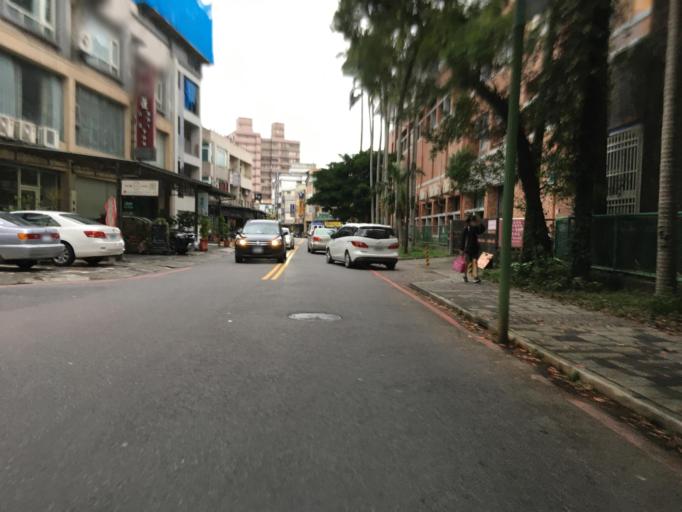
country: TW
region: Taiwan
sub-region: Yilan
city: Yilan
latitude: 24.6783
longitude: 121.7603
